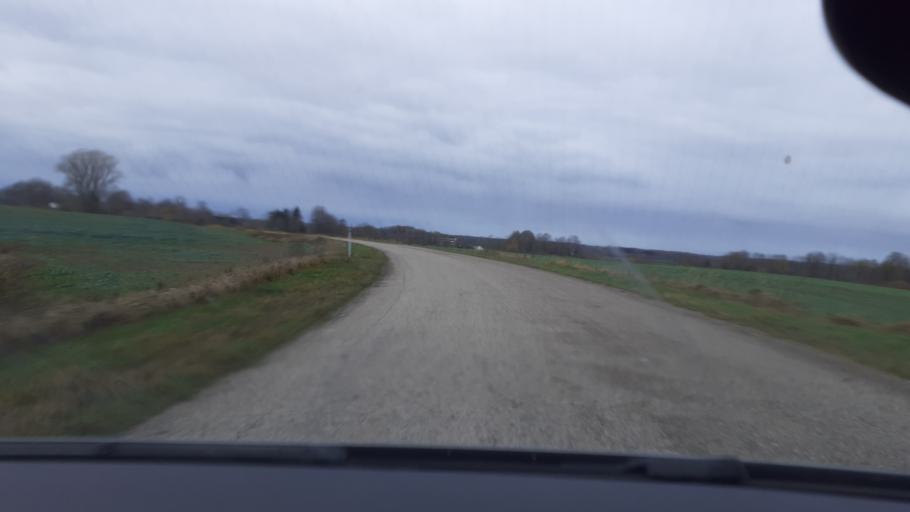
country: LV
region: Aizpute
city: Aizpute
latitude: 56.7838
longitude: 21.7667
